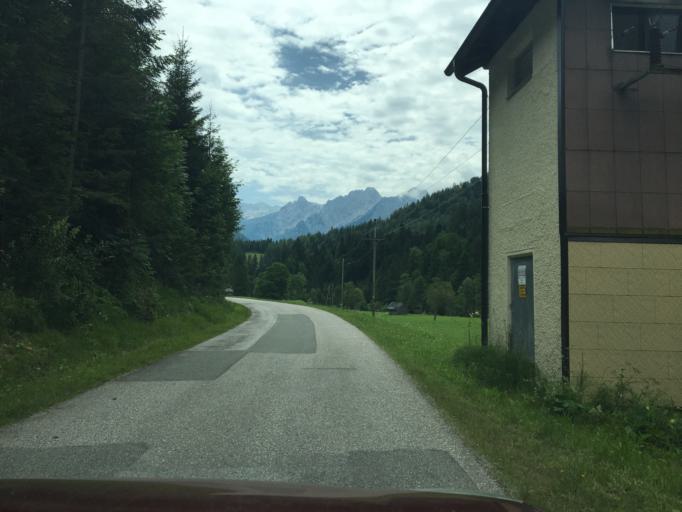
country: AT
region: Salzburg
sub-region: Politischer Bezirk Hallein
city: Scheffau am Tennengebirge
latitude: 47.6093
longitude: 13.2643
